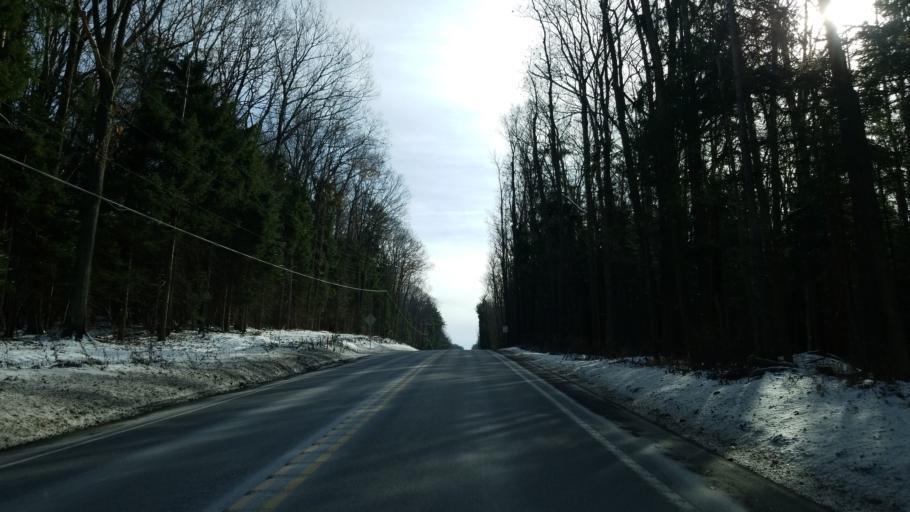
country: US
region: Pennsylvania
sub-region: Clearfield County
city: Clearfield
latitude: 41.1442
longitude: -78.5443
